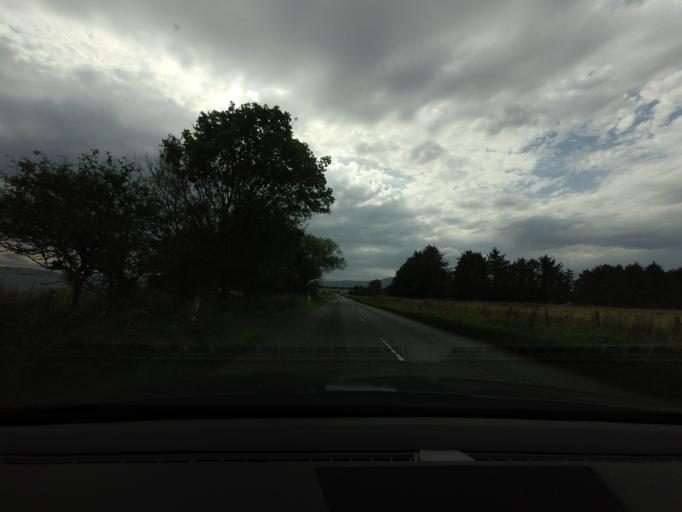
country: GB
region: Scotland
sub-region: Highland
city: Alness
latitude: 57.6911
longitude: -4.2214
